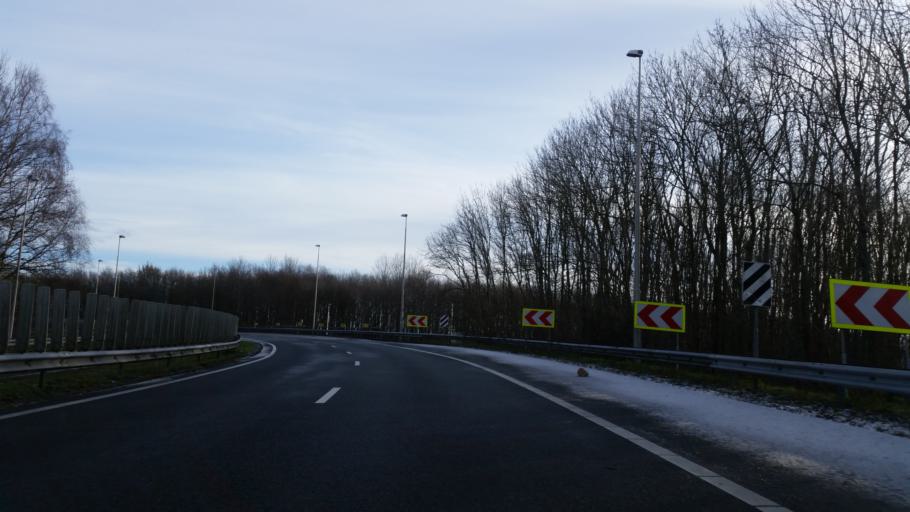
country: NL
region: Flevoland
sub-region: Gemeente Noordoostpolder
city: Emmeloord
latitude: 52.6914
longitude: 5.7737
